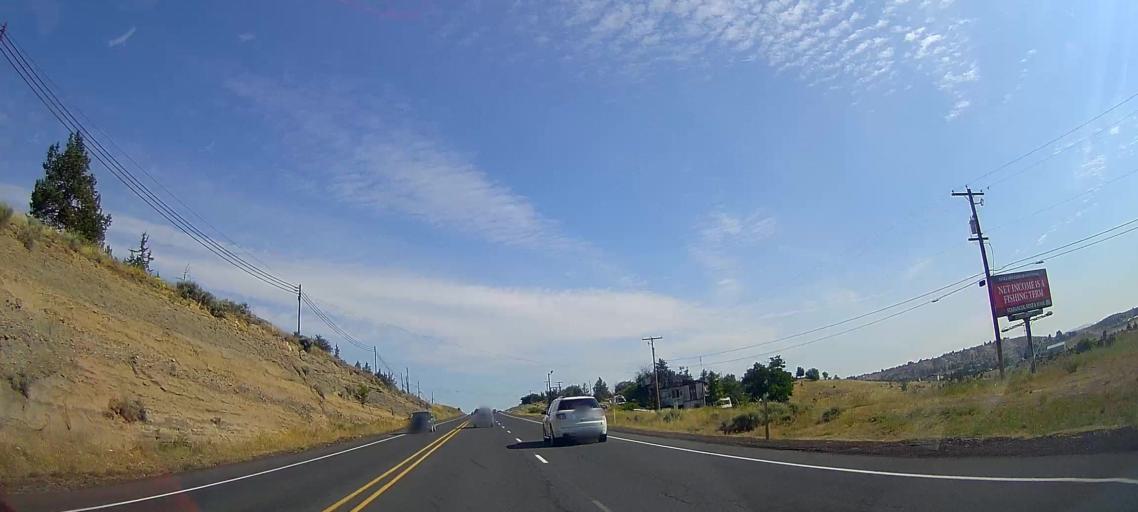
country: US
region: Oregon
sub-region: Jefferson County
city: Madras
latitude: 44.6483
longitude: -121.1292
